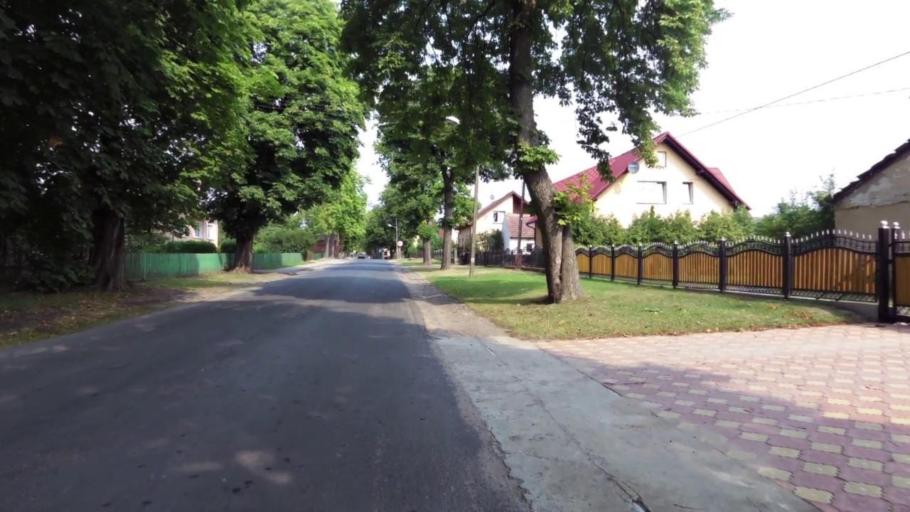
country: PL
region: West Pomeranian Voivodeship
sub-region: Powiat mysliborski
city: Debno
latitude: 52.8502
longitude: 14.6735
